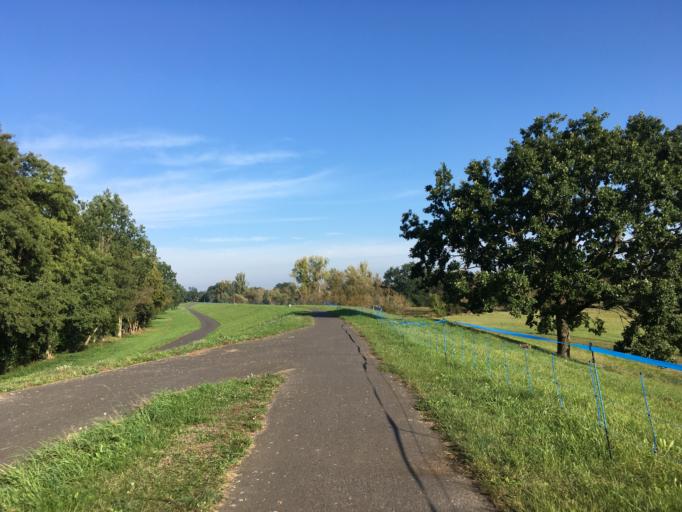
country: PL
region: Lubusz
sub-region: Powiat gorzowski
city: Kostrzyn nad Odra
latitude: 52.5655
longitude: 14.6232
